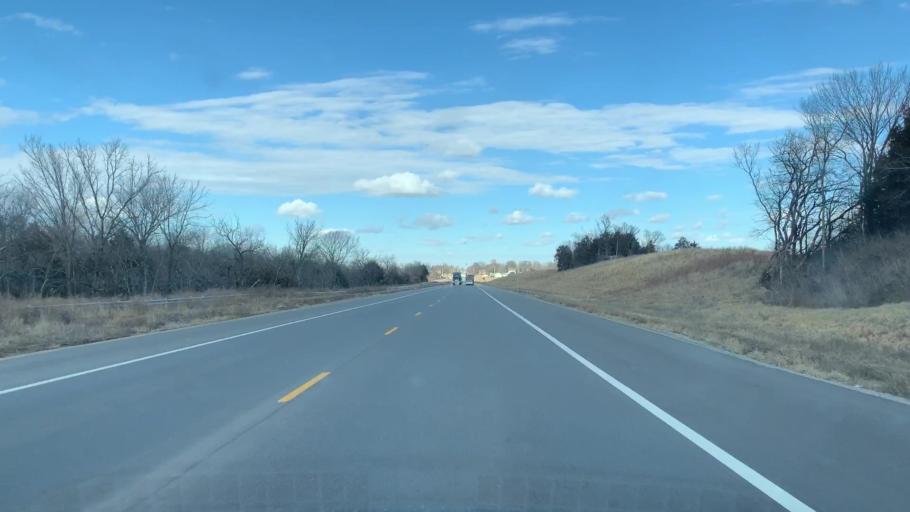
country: US
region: Kansas
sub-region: Crawford County
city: Pittsburg
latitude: 37.3316
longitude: -94.8321
